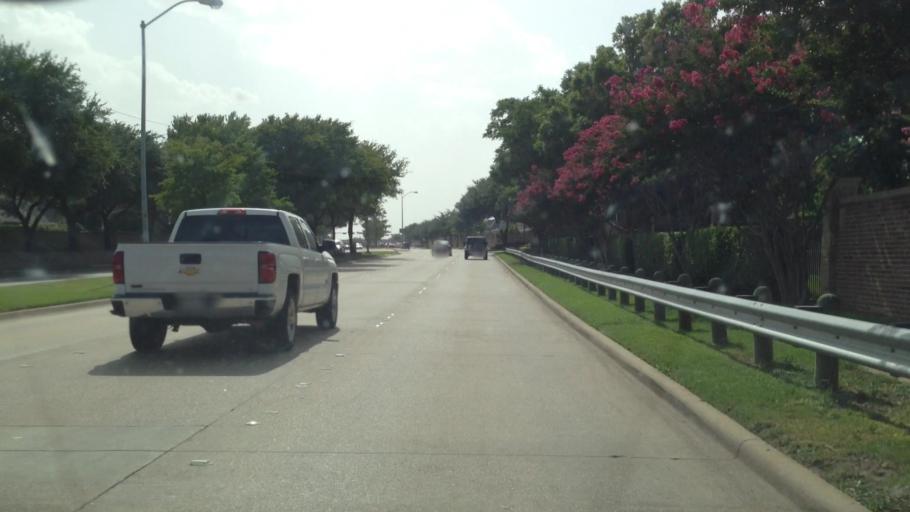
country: US
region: Texas
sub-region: Dallas County
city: Addison
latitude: 33.0279
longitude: -96.8218
